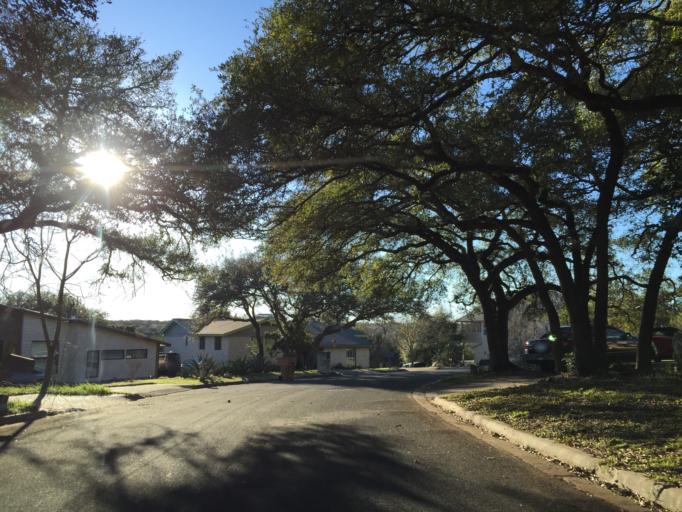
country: US
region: Texas
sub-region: Williamson County
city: Jollyville
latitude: 30.4380
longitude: -97.7909
